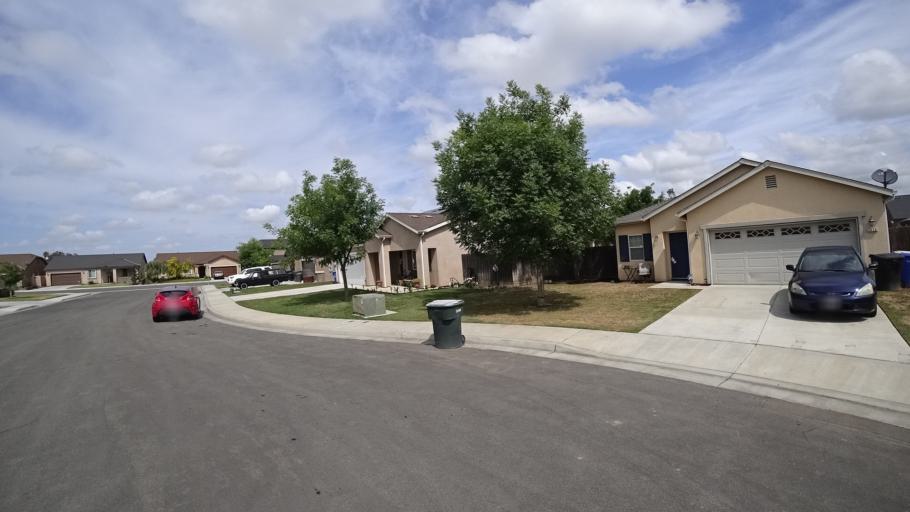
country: US
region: California
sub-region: Kings County
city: Hanford
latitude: 36.3062
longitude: -119.6669
